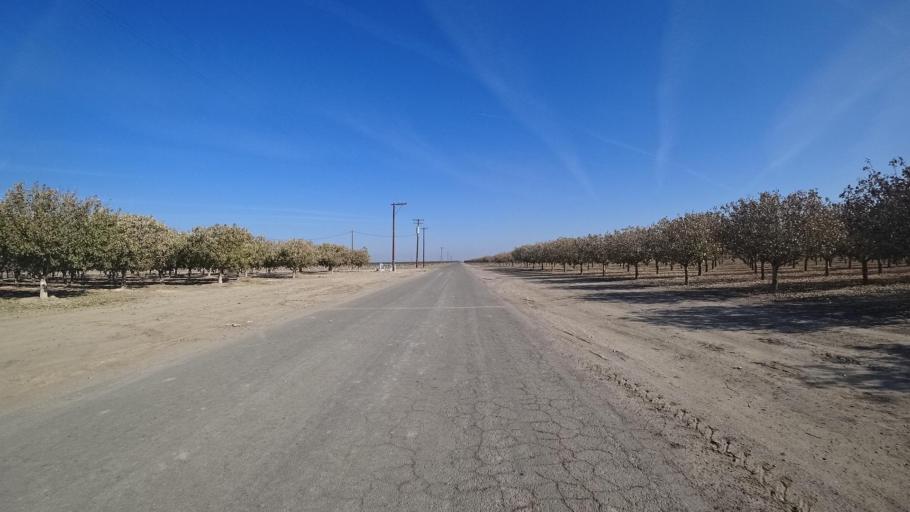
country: US
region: California
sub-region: Kern County
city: Wasco
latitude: 35.6886
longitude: -119.4250
